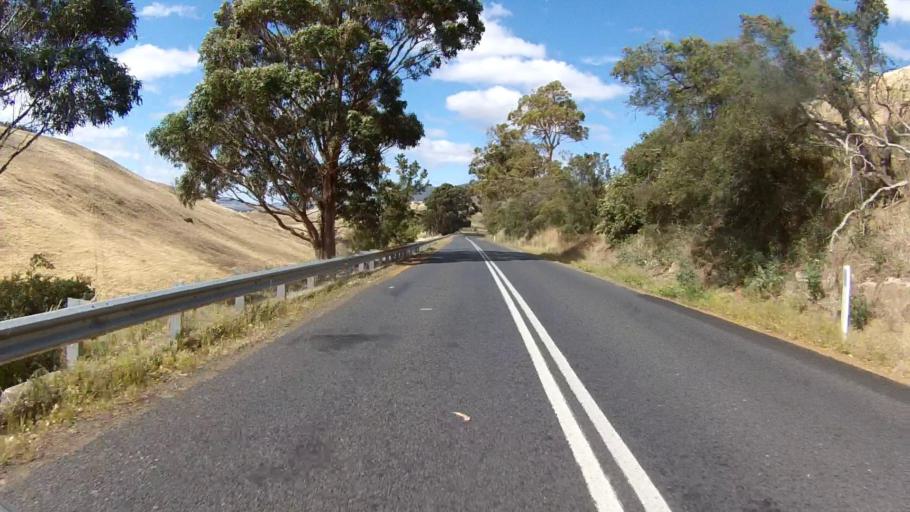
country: AU
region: Tasmania
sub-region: Brighton
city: Bridgewater
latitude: -42.5627
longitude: 147.3912
